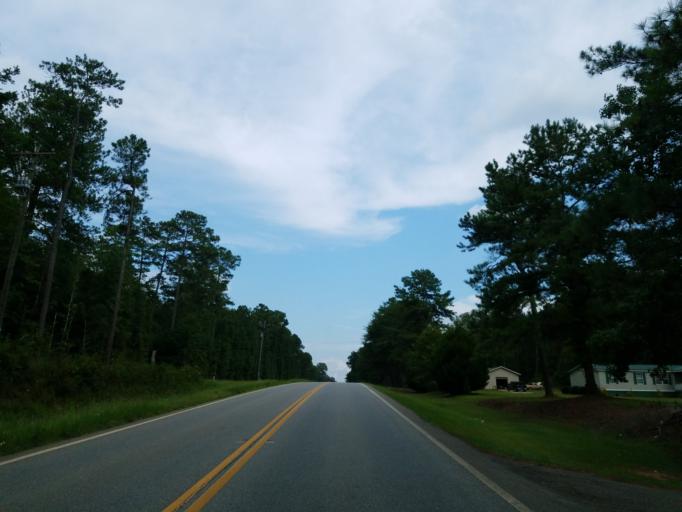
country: US
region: Georgia
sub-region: Dooly County
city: Unadilla
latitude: 32.3240
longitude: -83.7212
